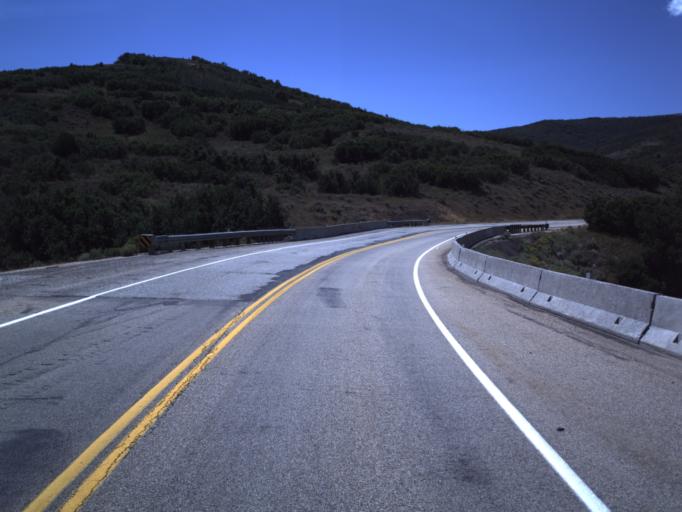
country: US
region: Utah
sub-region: Wasatch County
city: Heber
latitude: 40.5910
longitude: -111.3776
